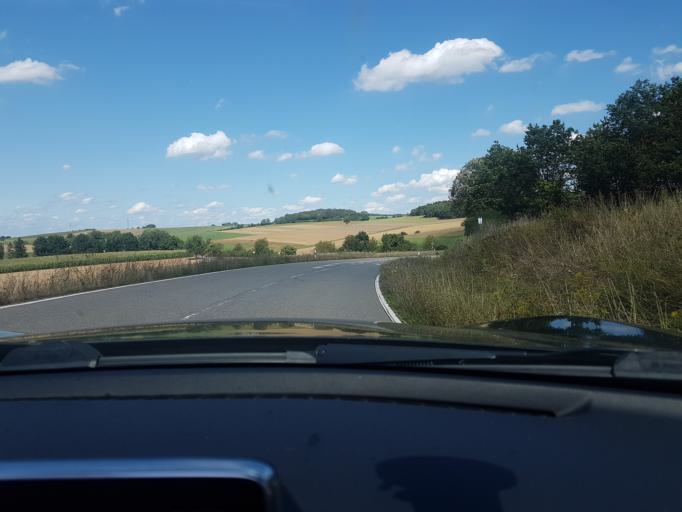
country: DE
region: Baden-Wuerttemberg
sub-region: Karlsruhe Region
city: Billigheim
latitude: 49.3385
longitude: 9.2811
